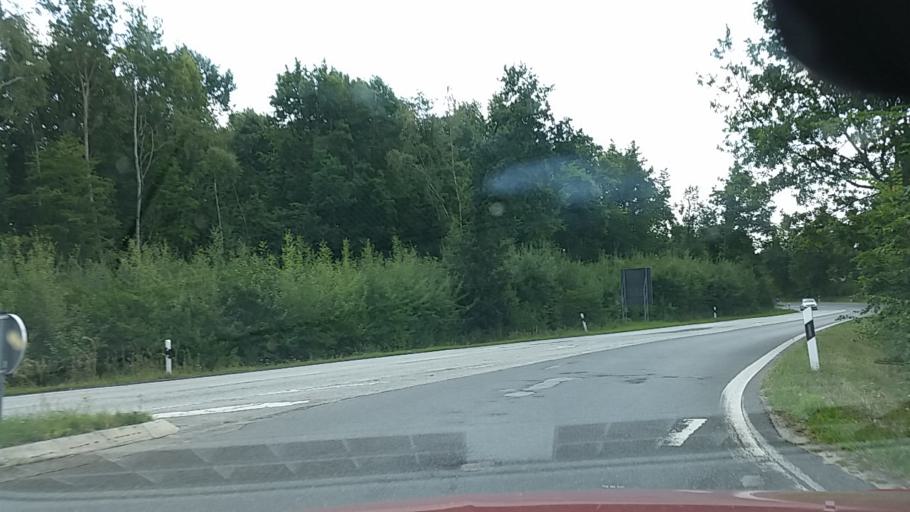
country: DE
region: Schleswig-Holstein
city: Reinbek
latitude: 53.5317
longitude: 10.2282
